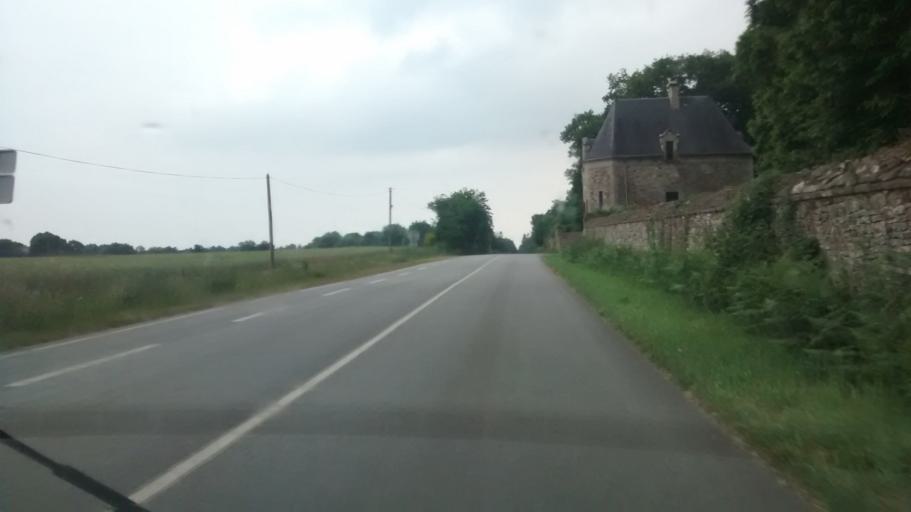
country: FR
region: Brittany
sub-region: Departement du Morbihan
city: Molac
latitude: 47.7678
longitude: -2.4344
